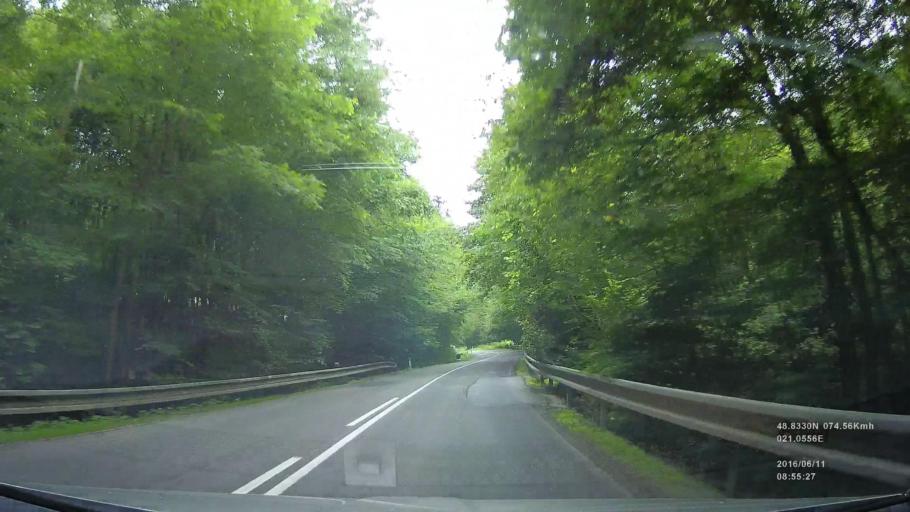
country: SK
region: Kosicky
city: Gelnica
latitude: 48.8135
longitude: 21.0924
